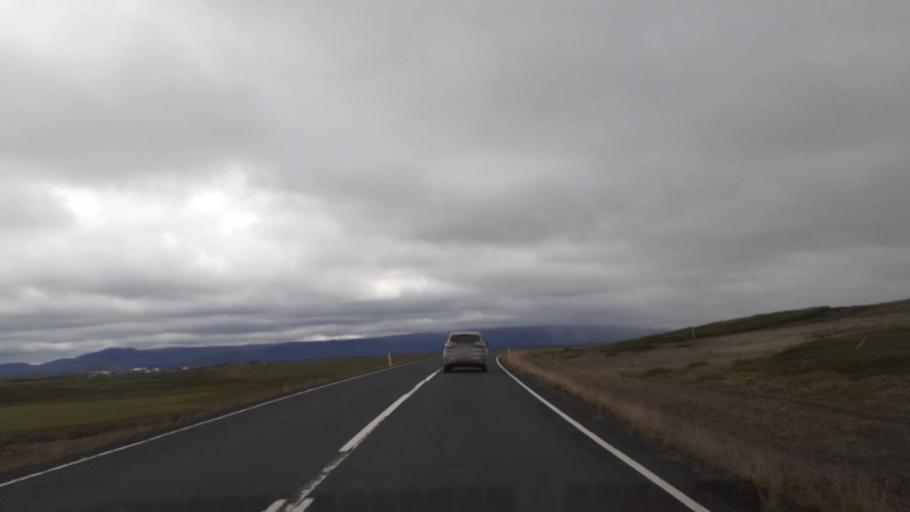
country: IS
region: Northeast
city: Laugar
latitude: 65.5766
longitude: -17.0919
